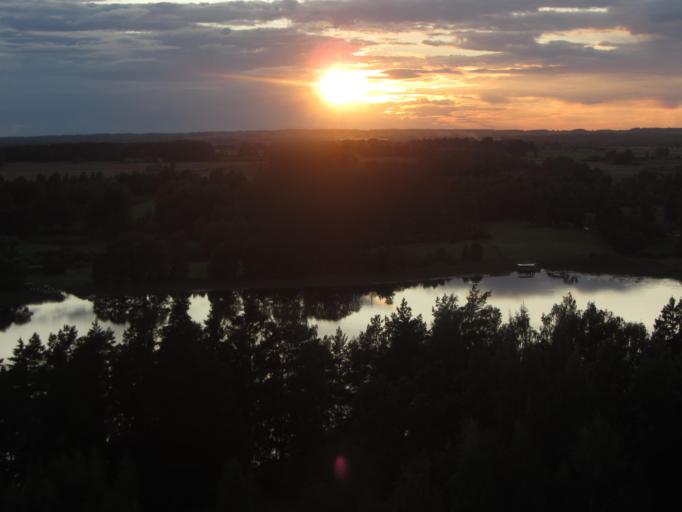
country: LT
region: Panevezys
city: Rokiskis
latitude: 55.8411
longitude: 25.8384
